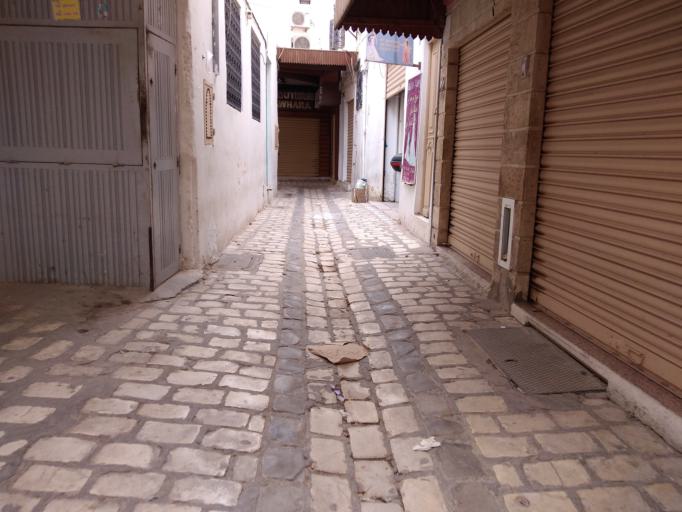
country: TN
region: Safaqis
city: Sfax
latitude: 34.7355
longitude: 10.7600
